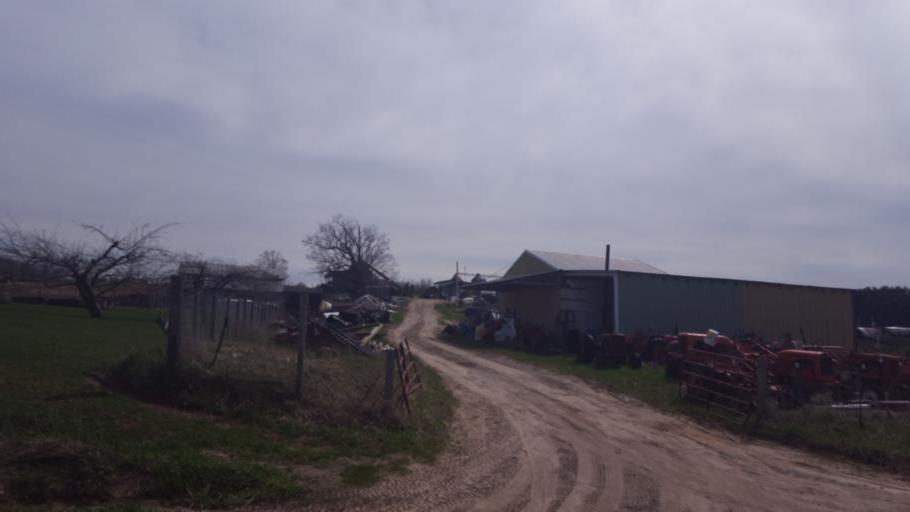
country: US
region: Michigan
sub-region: Gladwin County
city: Gladwin
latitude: 43.9878
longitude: -84.5328
